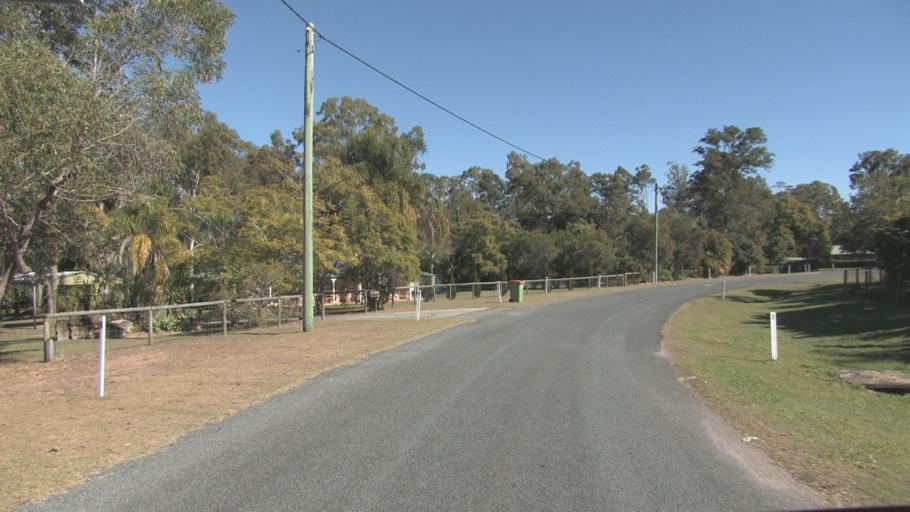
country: AU
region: Queensland
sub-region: Logan
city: Park Ridge South
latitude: -27.7294
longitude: 153.0469
